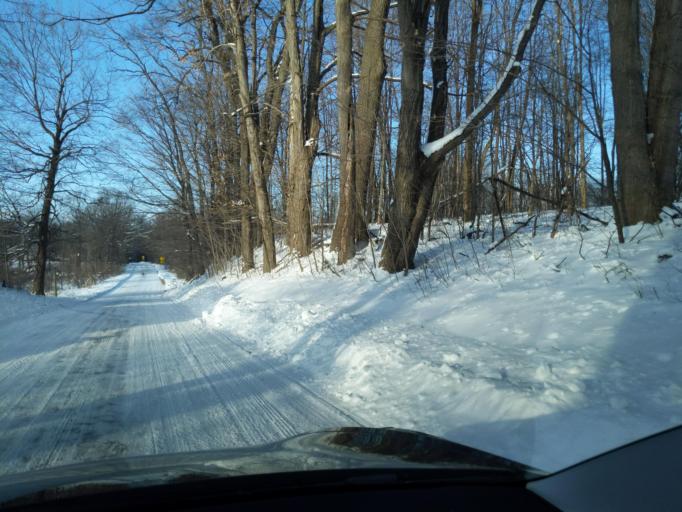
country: US
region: Michigan
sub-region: Ingham County
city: Stockbridge
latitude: 42.4578
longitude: -84.1042
